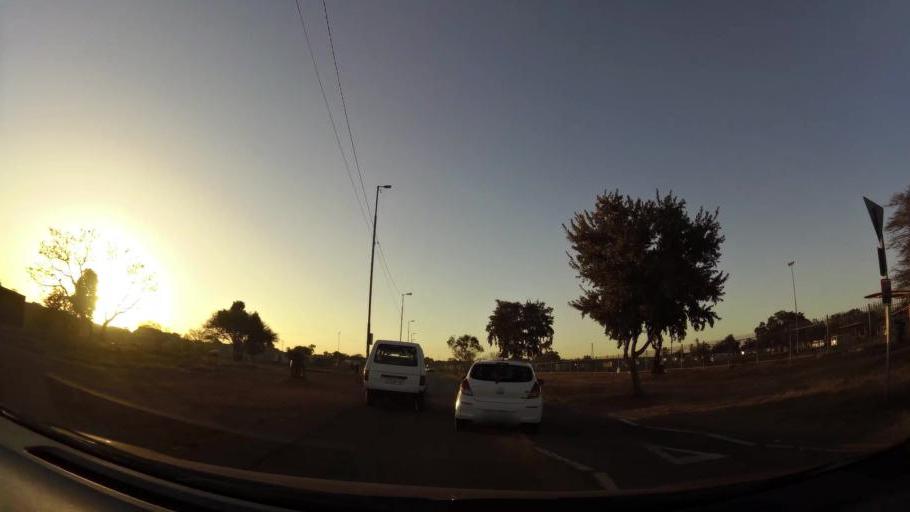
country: ZA
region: Gauteng
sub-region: City of Tshwane Metropolitan Municipality
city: Mabopane
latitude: -25.5824
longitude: 28.0880
